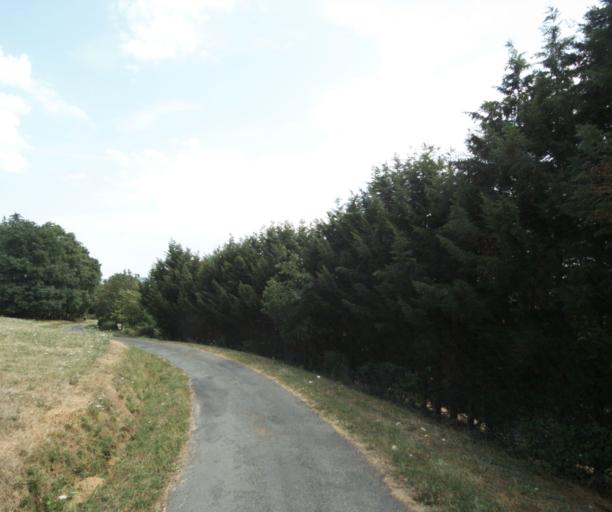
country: FR
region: Bourgogne
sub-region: Departement de Saone-et-Loire
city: Gueugnon
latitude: 46.6061
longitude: 4.0339
